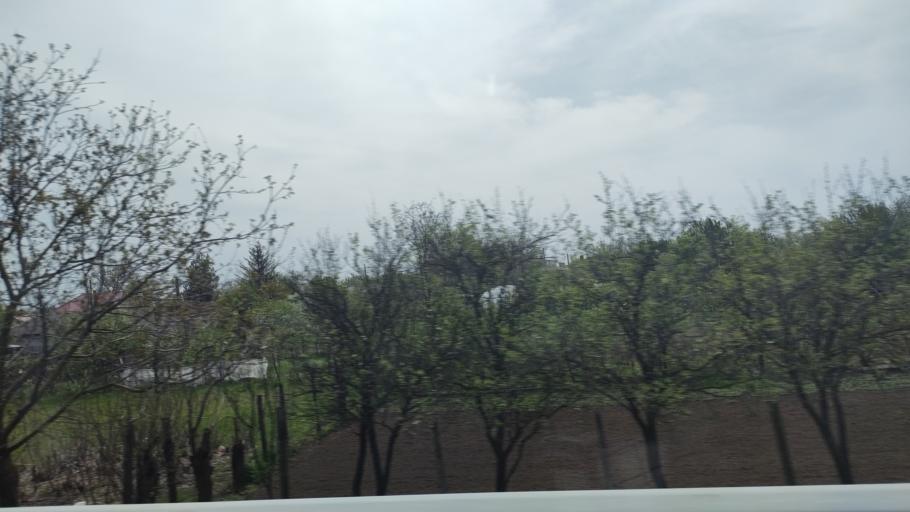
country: RO
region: Constanta
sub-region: Comuna Cobadin
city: Cobadin
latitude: 44.0702
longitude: 28.2237
